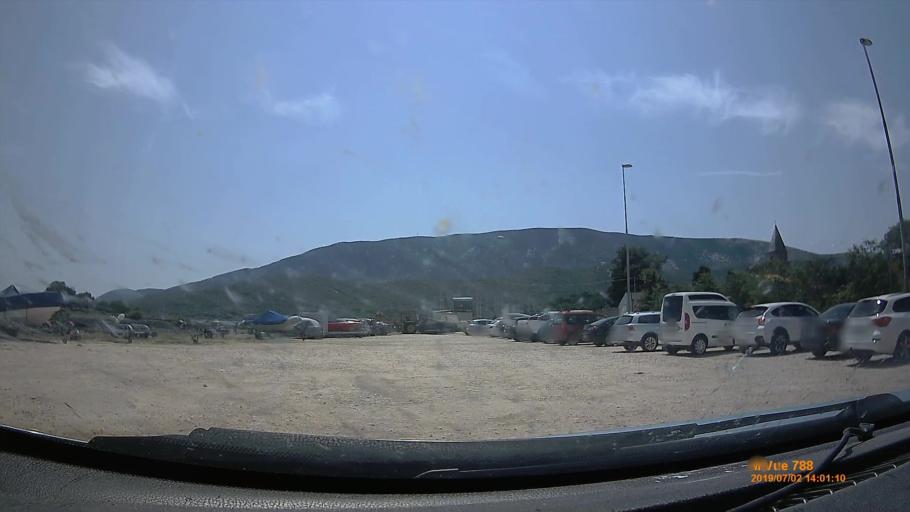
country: HR
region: Primorsko-Goranska
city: Mali Losinj
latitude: 44.6941
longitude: 14.3960
